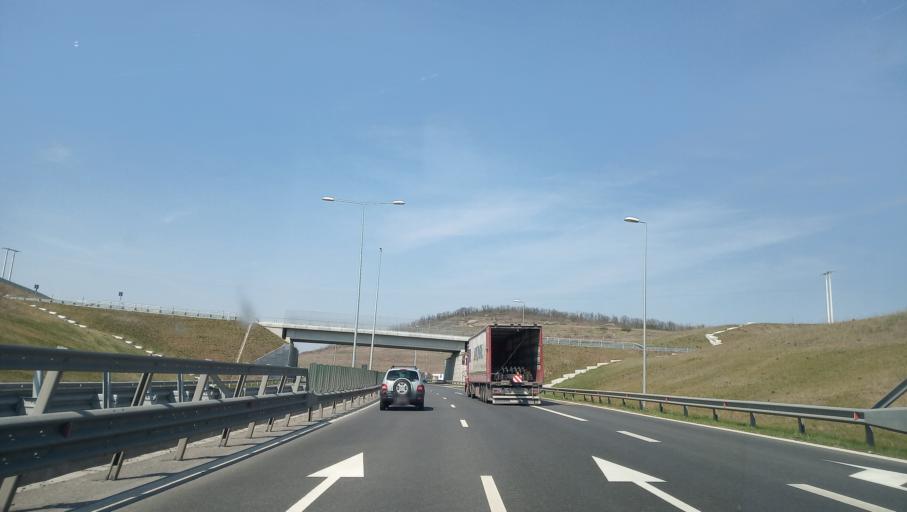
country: RO
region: Alba
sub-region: Comuna Miraslau
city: Miraslau
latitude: 46.3421
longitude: 23.7333
